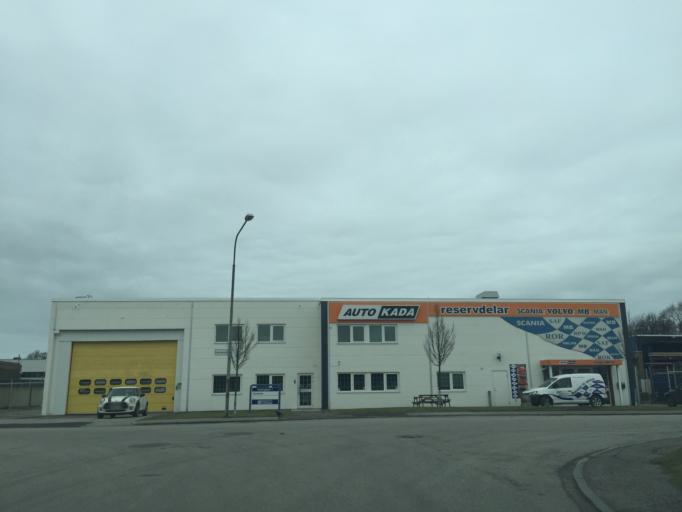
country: SE
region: Skane
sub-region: Burlovs Kommun
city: Arloev
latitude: 55.6036
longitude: 13.0638
